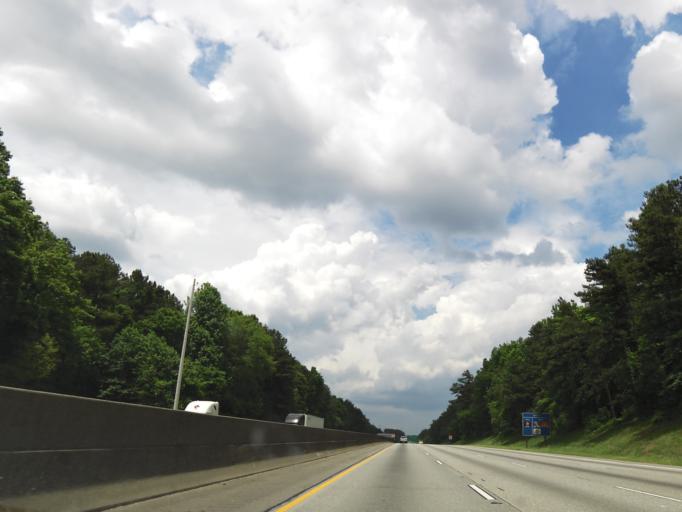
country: US
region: Georgia
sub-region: Fulton County
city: East Point
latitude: 33.7392
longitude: -84.5003
